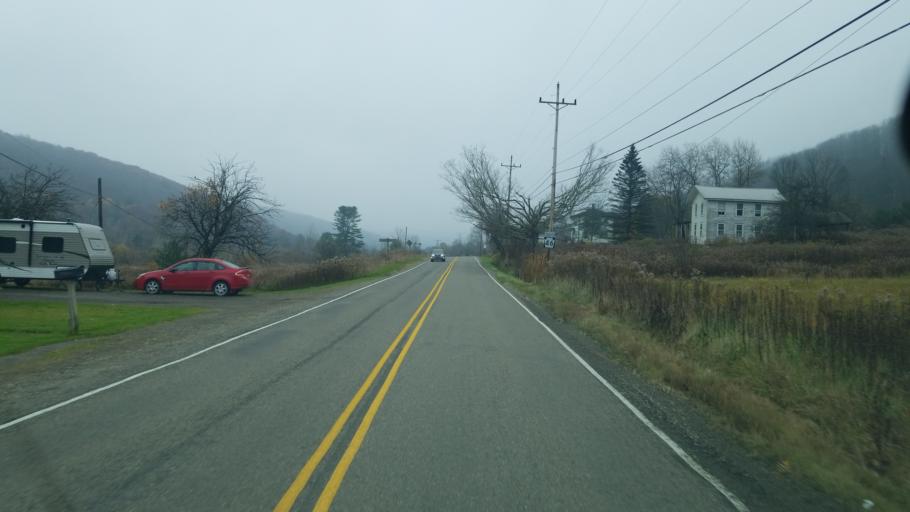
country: US
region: Pennsylvania
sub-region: McKean County
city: Smethport
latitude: 41.8825
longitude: -78.4931
